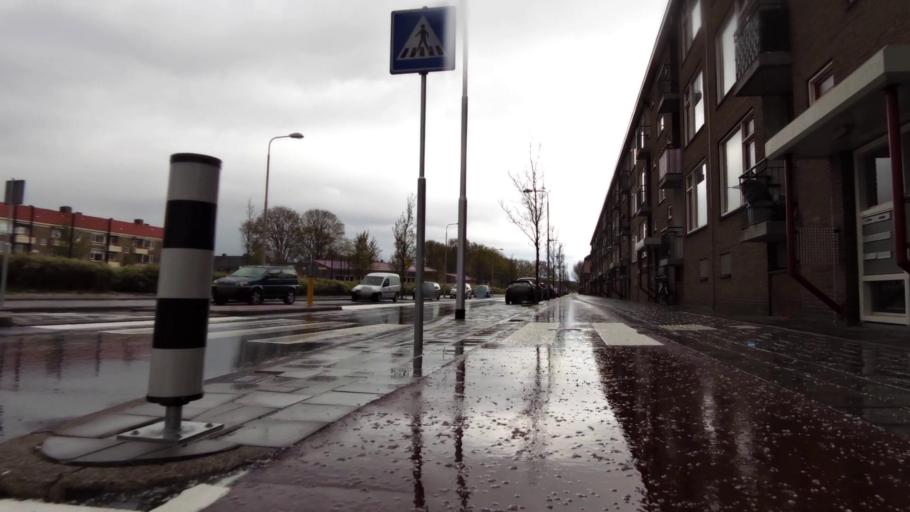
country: NL
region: North Holland
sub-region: Gemeente Velsen
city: Velsen-Zuid
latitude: 52.4536
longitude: 4.5944
